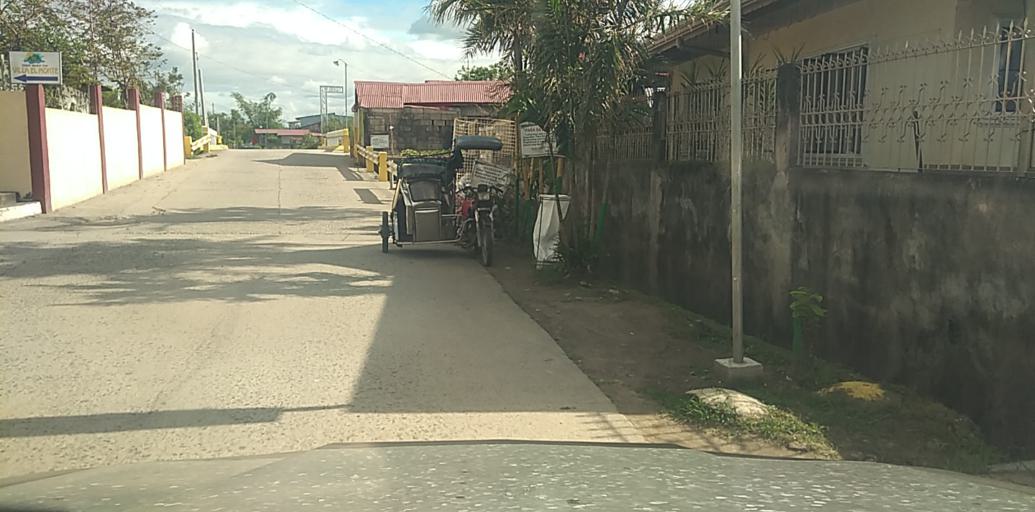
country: PH
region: Central Luzon
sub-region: Province of Pampanga
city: Panlinlang
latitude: 15.1866
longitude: 120.6934
